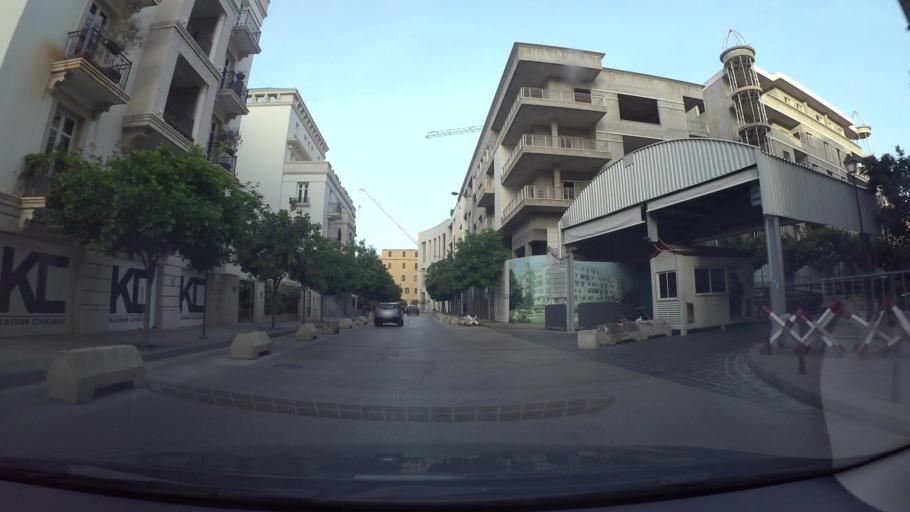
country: LB
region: Beyrouth
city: Beirut
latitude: 33.8983
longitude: 35.4989
